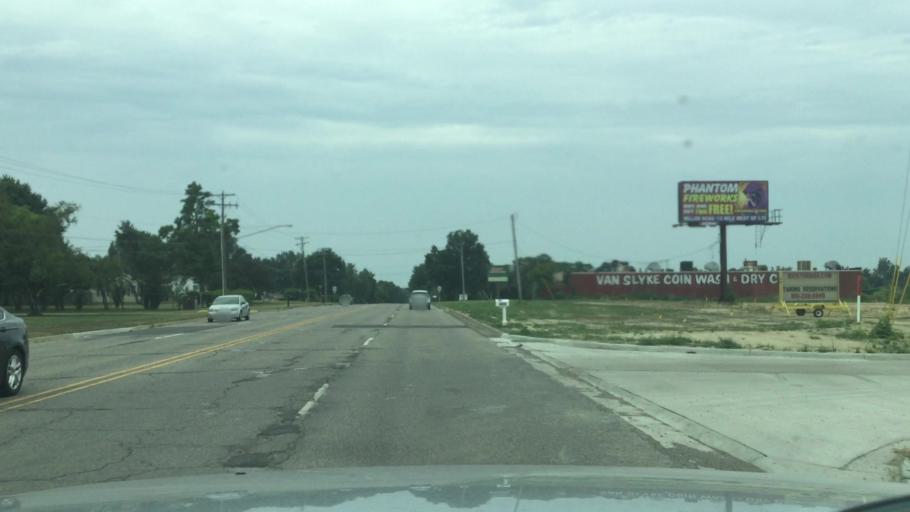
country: US
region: Michigan
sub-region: Genesee County
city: Flint
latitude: 42.9713
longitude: -83.7129
